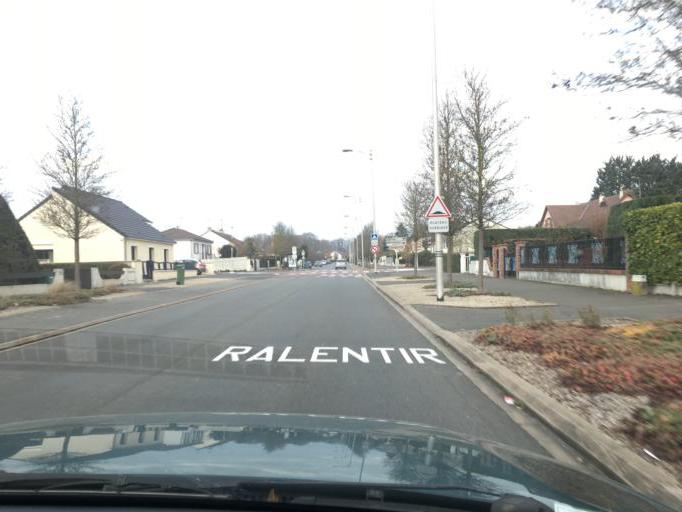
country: FR
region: Centre
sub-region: Departement du Loiret
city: Saran
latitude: 47.9487
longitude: 1.8839
